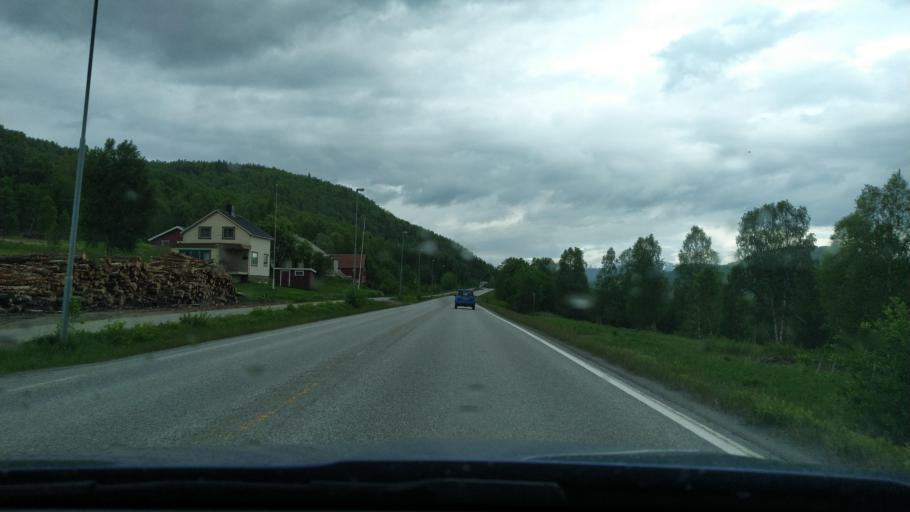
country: NO
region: Troms
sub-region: Malselv
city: Moen
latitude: 69.0181
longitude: 18.4854
